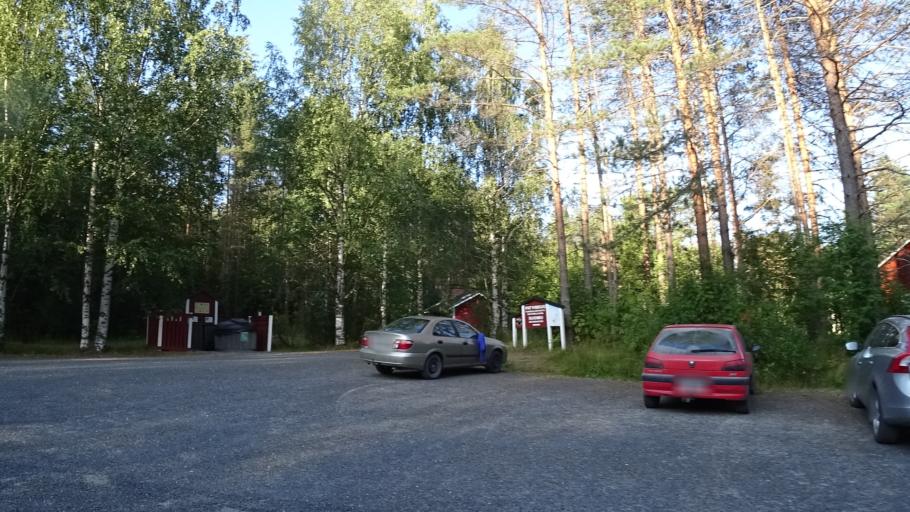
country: FI
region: North Karelia
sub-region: Joensuu
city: Ilomantsi
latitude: 63.1311
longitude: 30.7276
